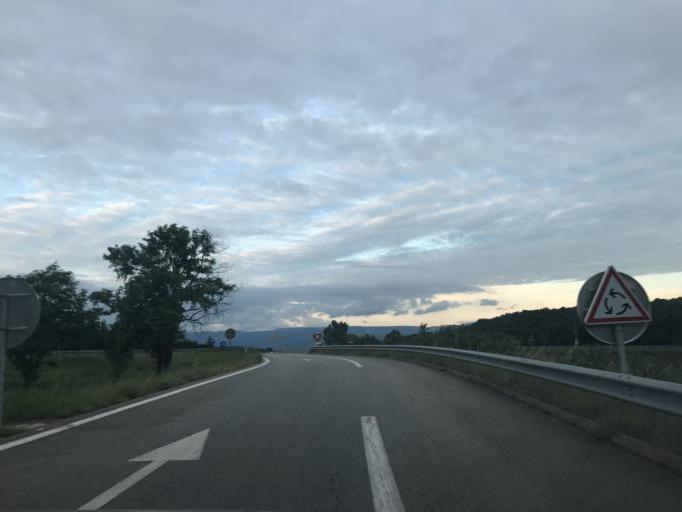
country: FR
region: Rhone-Alpes
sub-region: Departement de la Drome
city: Malissard
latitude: 44.9035
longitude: 4.9245
